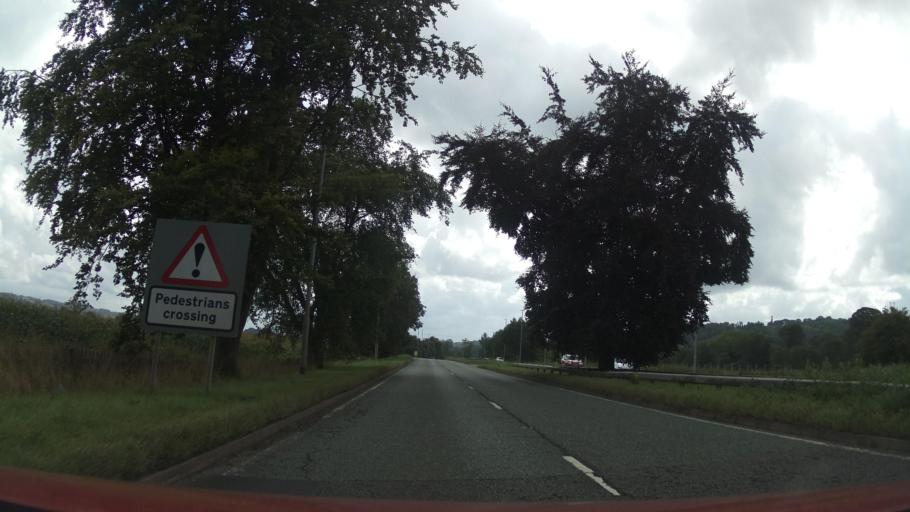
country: GB
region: England
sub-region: Staffordshire
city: Barlaston
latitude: 52.9571
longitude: -2.1936
